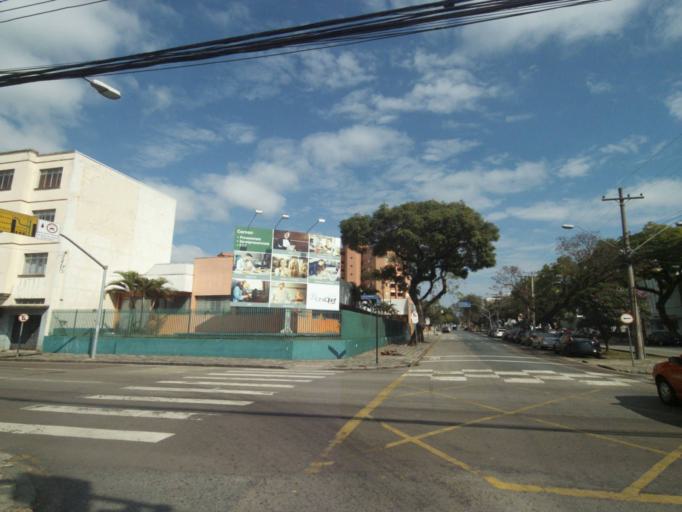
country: BR
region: Parana
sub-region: Curitiba
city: Curitiba
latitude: -25.4420
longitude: -49.2685
